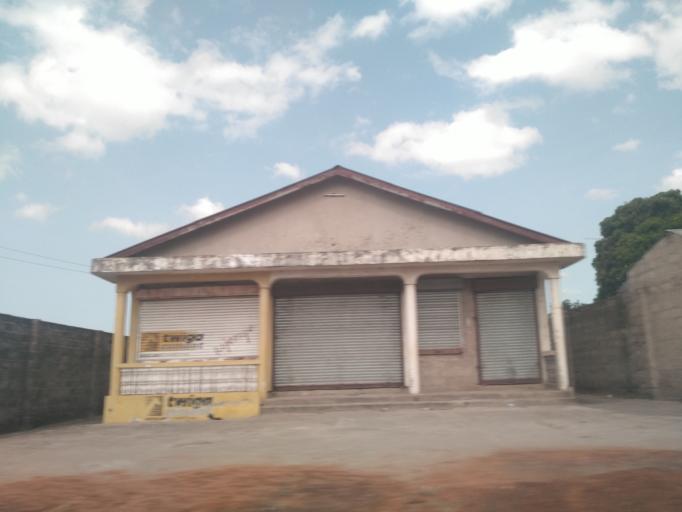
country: TZ
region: Dar es Salaam
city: Dar es Salaam
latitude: -6.8958
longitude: 39.2836
